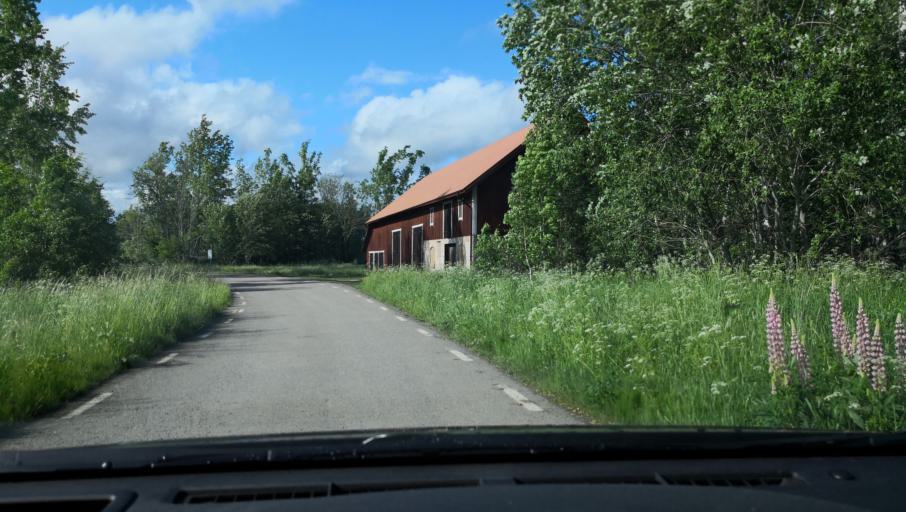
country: SE
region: OErebro
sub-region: Lindesbergs Kommun
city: Fellingsbro
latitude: 59.3363
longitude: 15.6866
